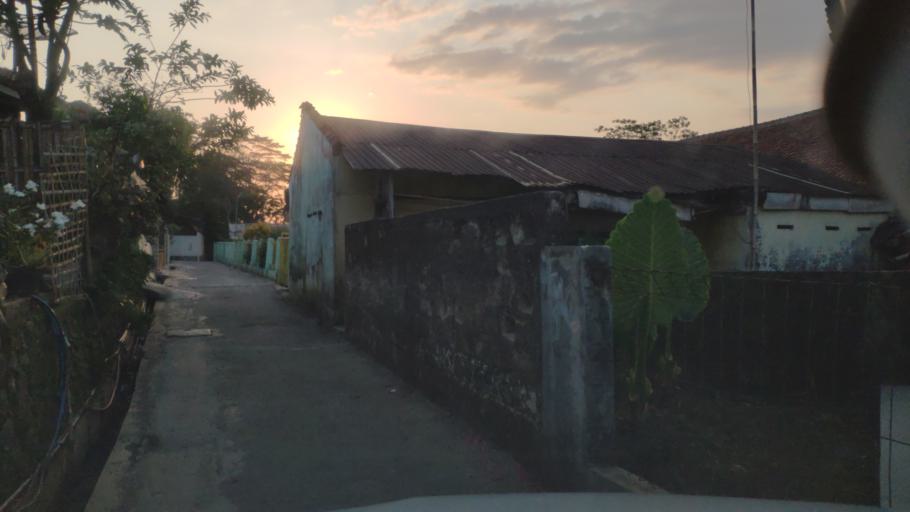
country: ID
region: Central Java
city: Wonosobo
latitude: -7.4057
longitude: 109.7298
